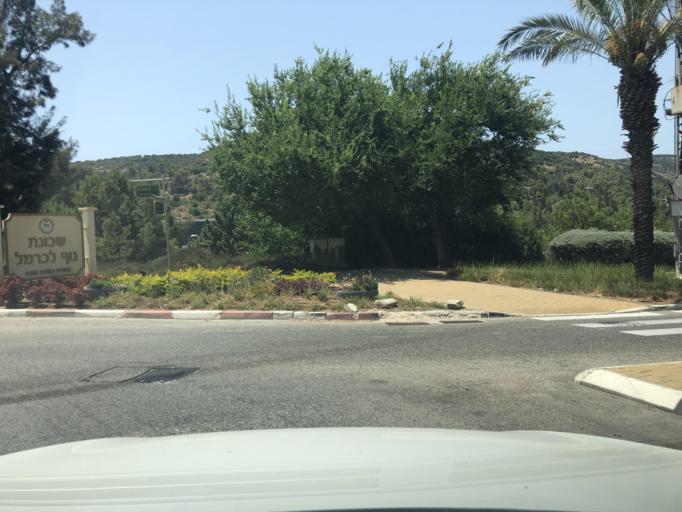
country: IL
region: Haifa
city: Daliyat el Karmil
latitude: 32.6587
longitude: 35.1068
